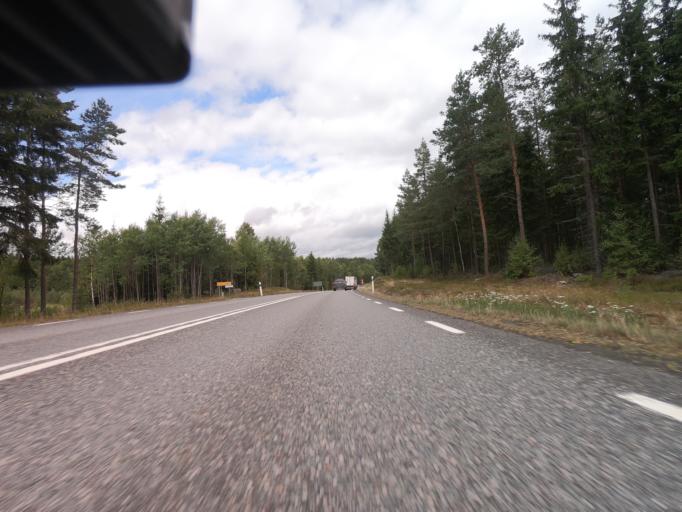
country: SE
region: Joenkoeping
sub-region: Vaggeryds Kommun
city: Vaggeryd
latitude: 57.5048
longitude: 14.2828
